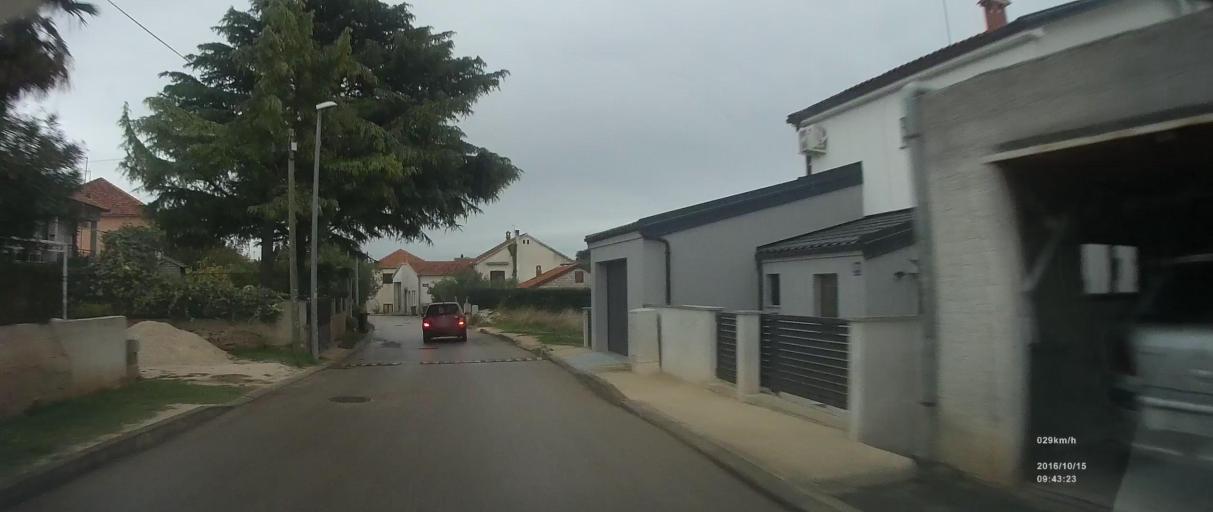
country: HR
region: Zadarska
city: Pakostane
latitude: 43.9111
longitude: 15.5043
